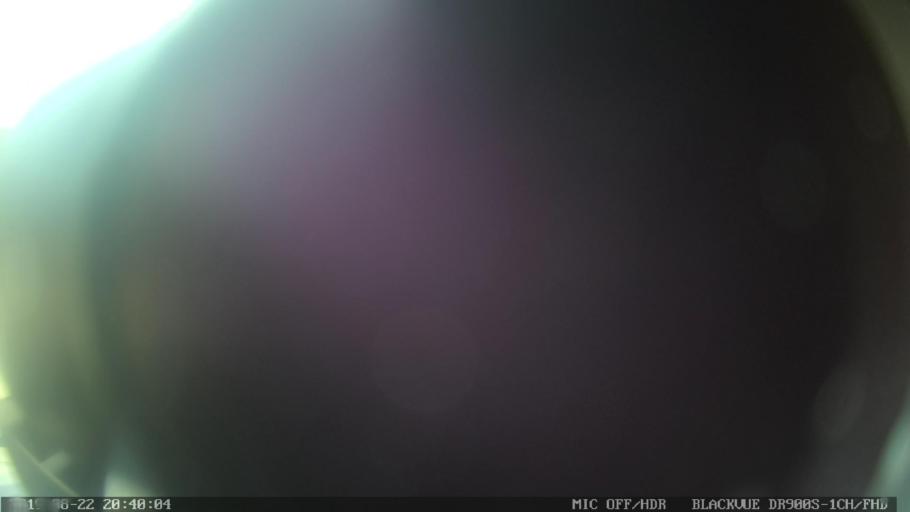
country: PT
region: Castelo Branco
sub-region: Proenca-A-Nova
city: Proenca-a-Nova
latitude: 39.6876
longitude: -7.7821
